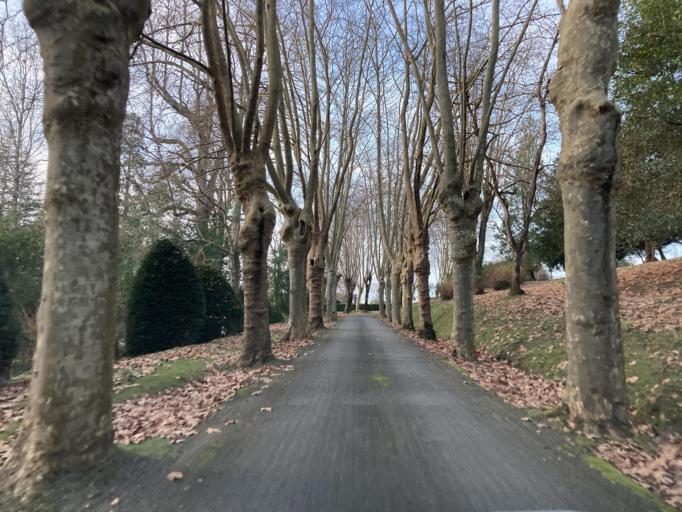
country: FR
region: Aquitaine
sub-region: Departement des Pyrenees-Atlantiques
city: Oloron-Sainte-Marie
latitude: 43.1916
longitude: -0.6001
